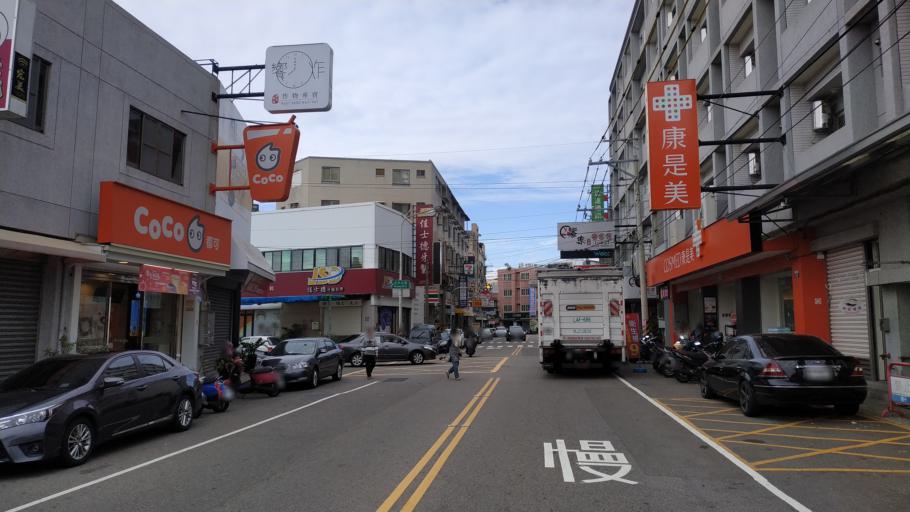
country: TW
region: Taiwan
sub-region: Taichung City
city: Taichung
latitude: 24.2287
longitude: 120.5740
